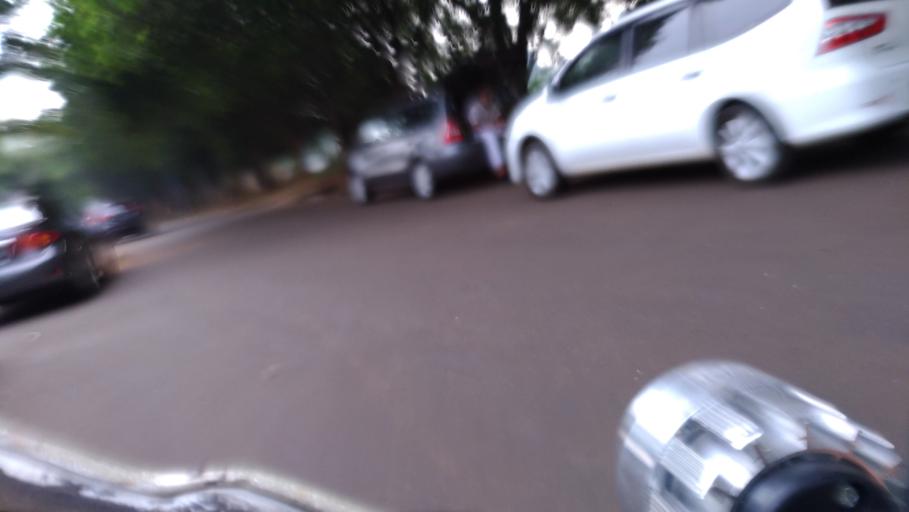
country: ID
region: West Java
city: Cileungsir
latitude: -6.3691
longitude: 106.8986
